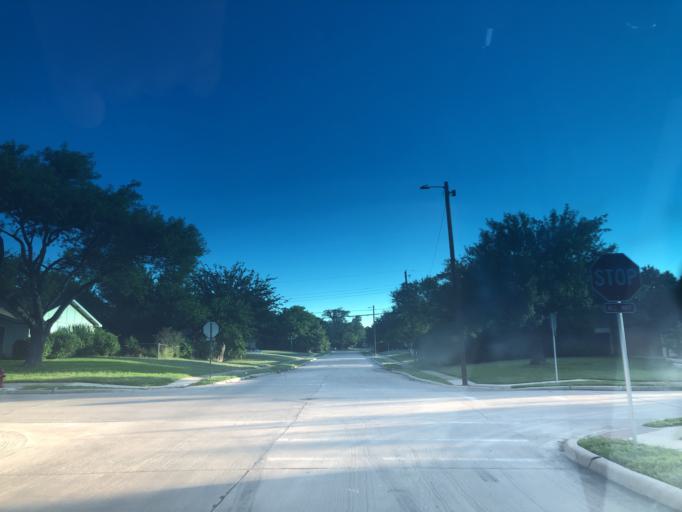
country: US
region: Texas
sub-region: Dallas County
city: Grand Prairie
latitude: 32.7016
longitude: -97.0117
